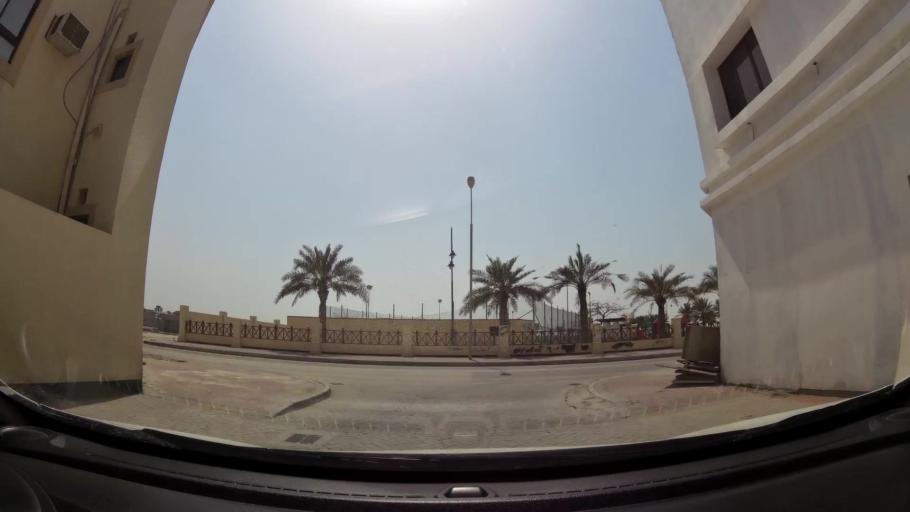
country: BH
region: Manama
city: Jidd Hafs
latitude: 26.2069
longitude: 50.4485
